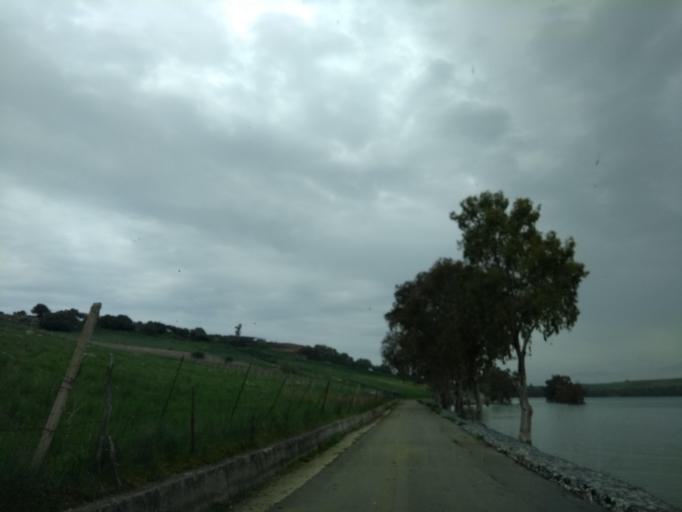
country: IT
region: Sicily
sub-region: Palermo
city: Partinico
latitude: 37.9929
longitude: 13.0823
